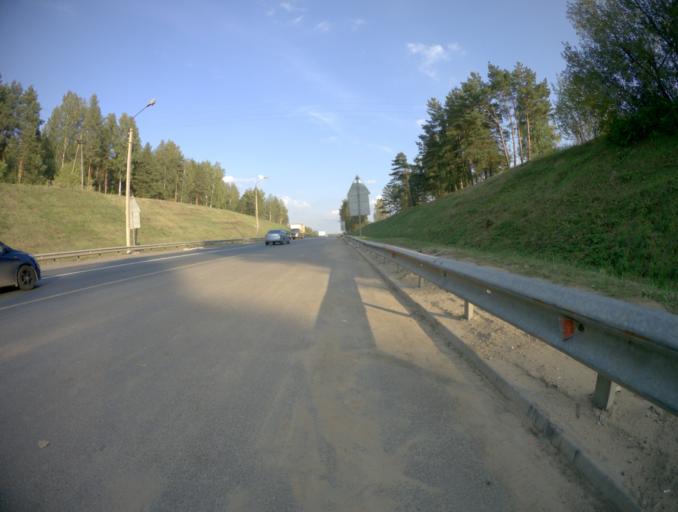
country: RU
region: Vladimir
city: Kameshkovo
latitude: 56.1954
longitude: 40.9145
